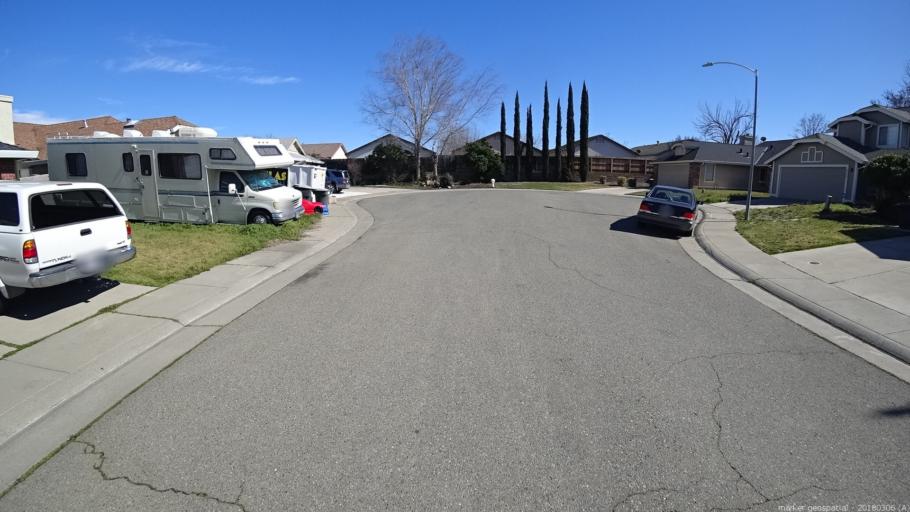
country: US
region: California
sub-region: Sacramento County
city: Vineyard
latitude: 38.4639
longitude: -121.3566
